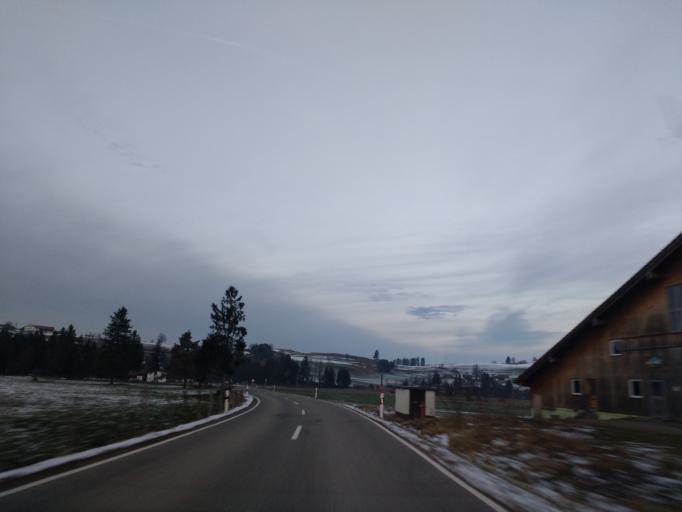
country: DE
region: Bavaria
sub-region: Swabia
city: Halblech
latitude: 47.6429
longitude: 10.8176
